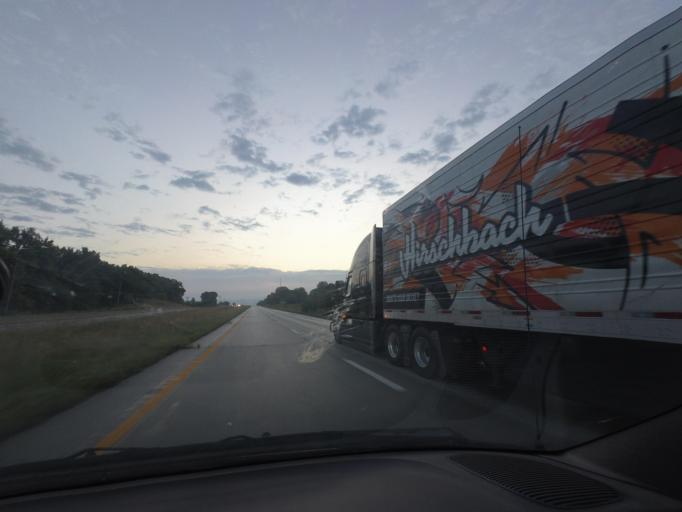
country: US
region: Missouri
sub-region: Macon County
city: Macon
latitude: 39.7478
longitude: -92.4867
